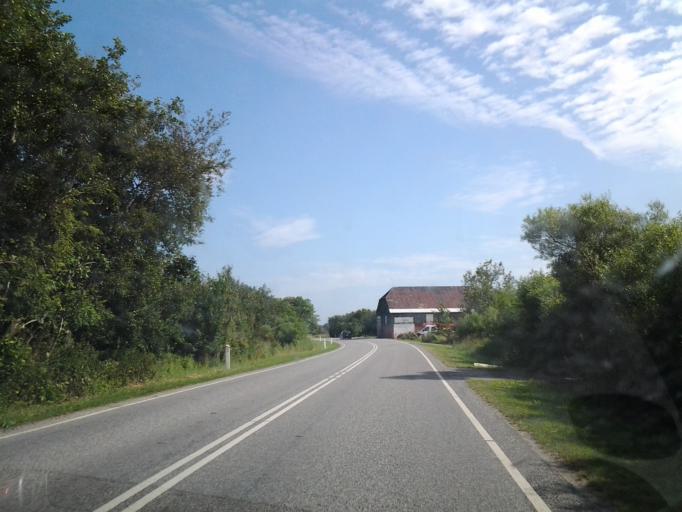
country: DE
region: Schleswig-Holstein
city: Neukirchen
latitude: 54.9136
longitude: 8.7412
